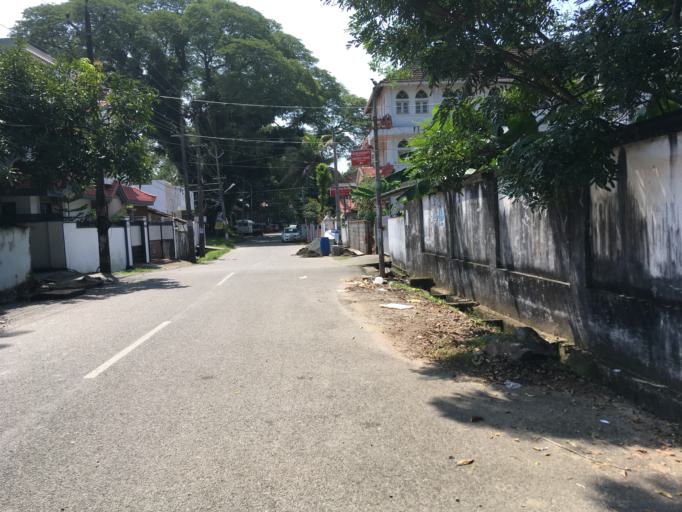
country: IN
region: Kerala
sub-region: Ernakulam
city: Cochin
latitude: 9.9622
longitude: 76.2407
